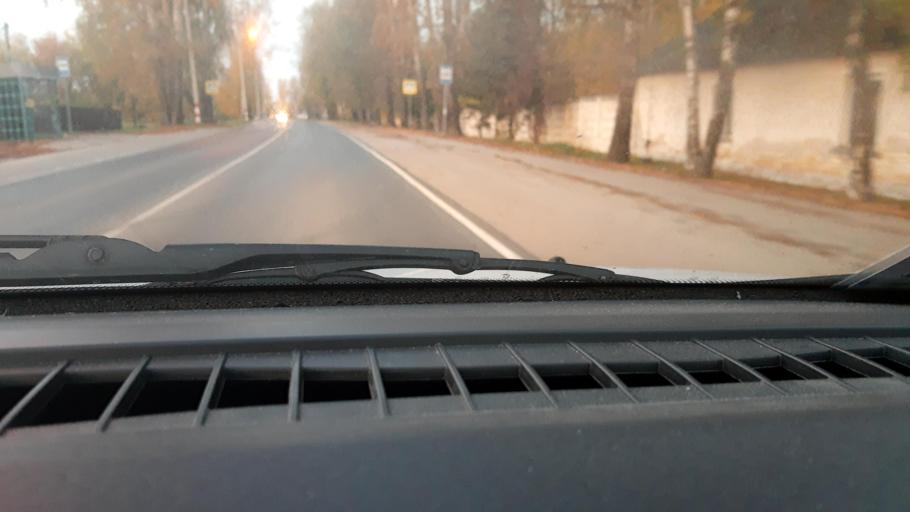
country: RU
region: Nizjnij Novgorod
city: Bor
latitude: 56.3794
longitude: 44.0358
